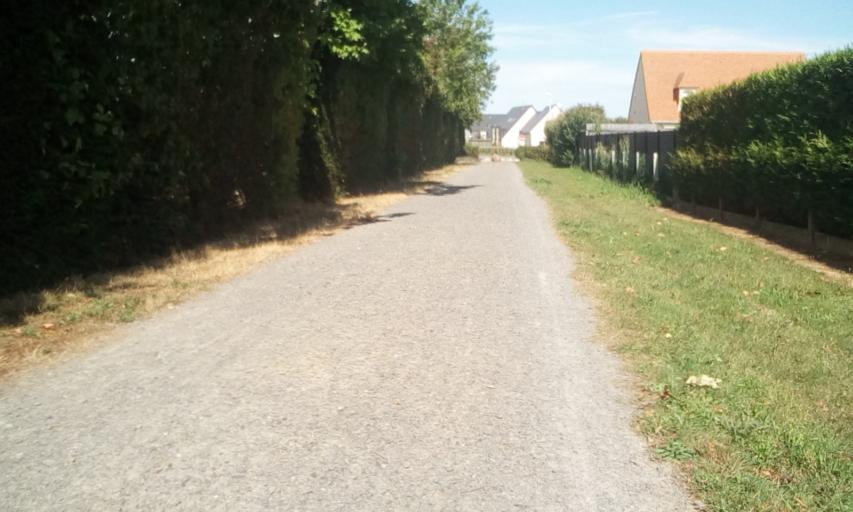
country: FR
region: Lower Normandy
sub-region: Departement du Calvados
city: Eterville
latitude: 49.1479
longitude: -0.4265
